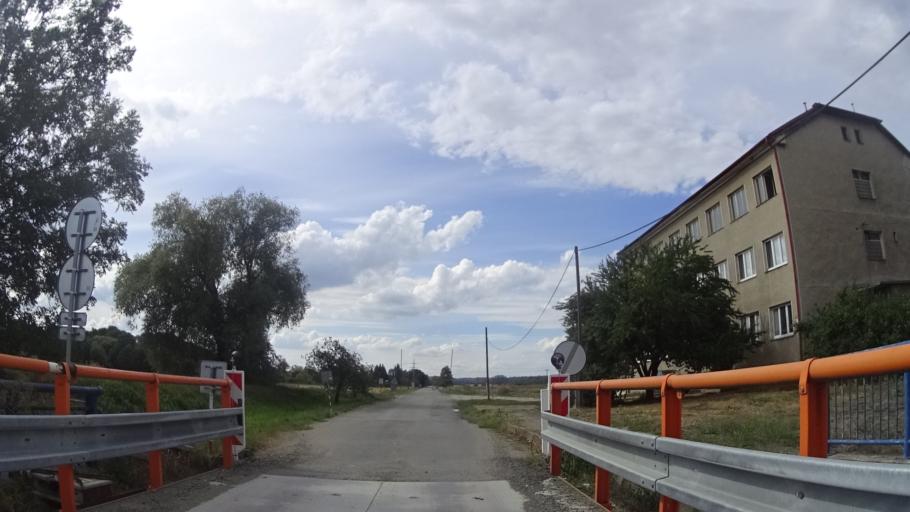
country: CZ
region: Olomoucky
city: Litovel
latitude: 49.7103
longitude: 17.0684
